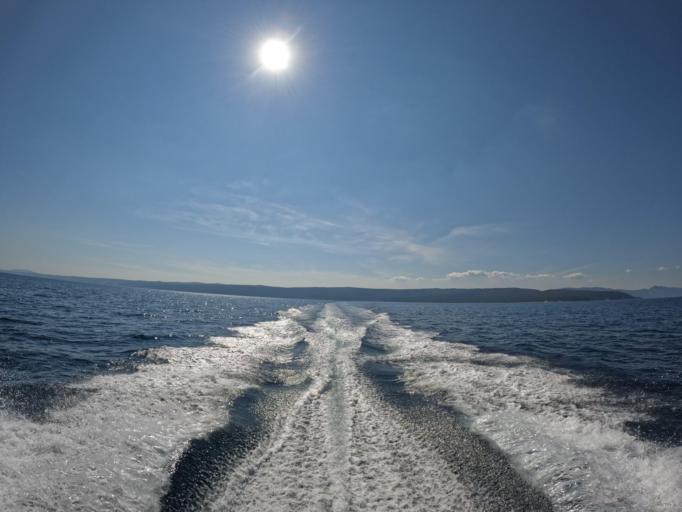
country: HR
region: Primorsko-Goranska
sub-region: Grad Krk
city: Krk
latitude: 44.9467
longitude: 14.5228
